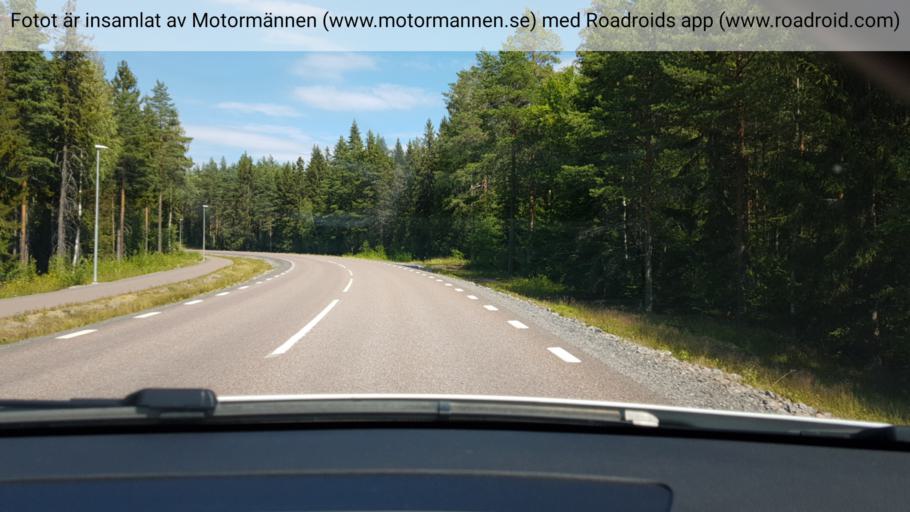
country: SE
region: Dalarna
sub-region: Borlange Kommun
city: Ornas
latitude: 60.5852
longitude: 15.5033
